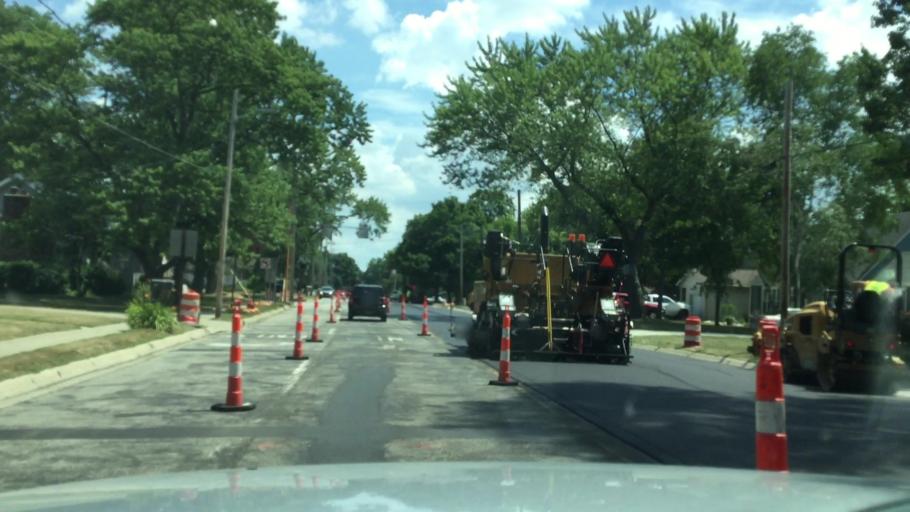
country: US
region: Michigan
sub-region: Genesee County
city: Flushing
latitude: 43.0641
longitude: -83.8334
